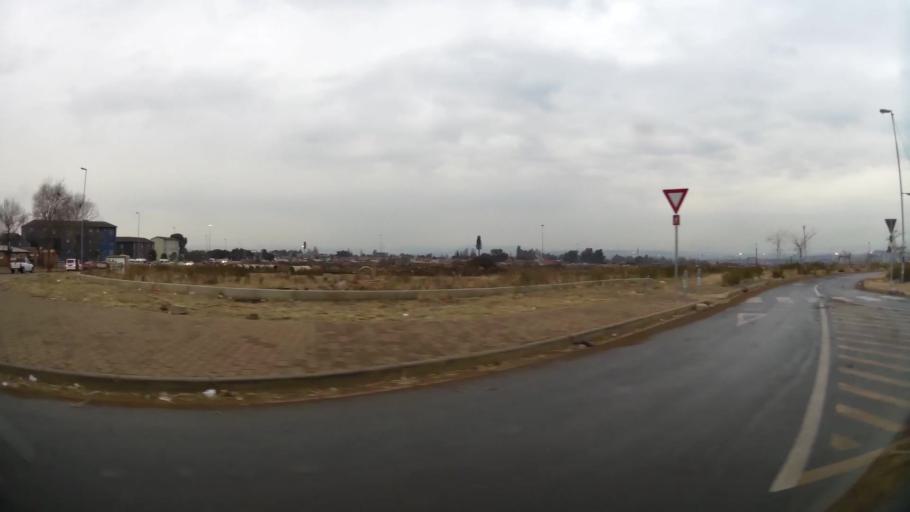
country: ZA
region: Gauteng
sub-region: City of Johannesburg Metropolitan Municipality
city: Soweto
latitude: -26.2458
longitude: 27.8640
